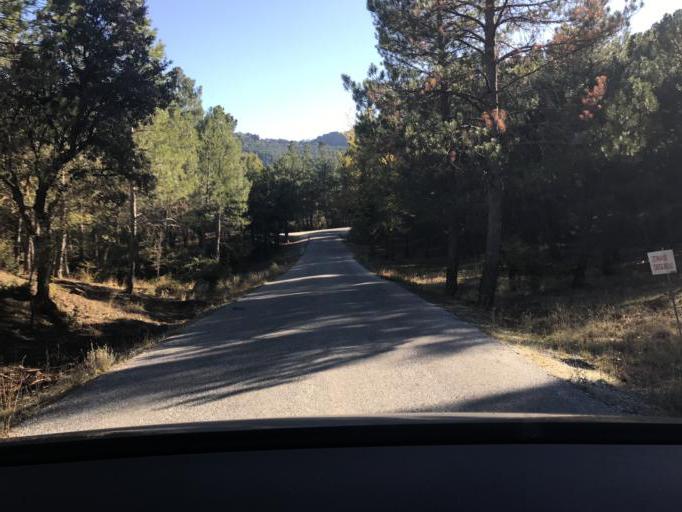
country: ES
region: Andalusia
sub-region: Provincia de Granada
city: Beas de Granada
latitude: 37.2965
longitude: -3.4733
